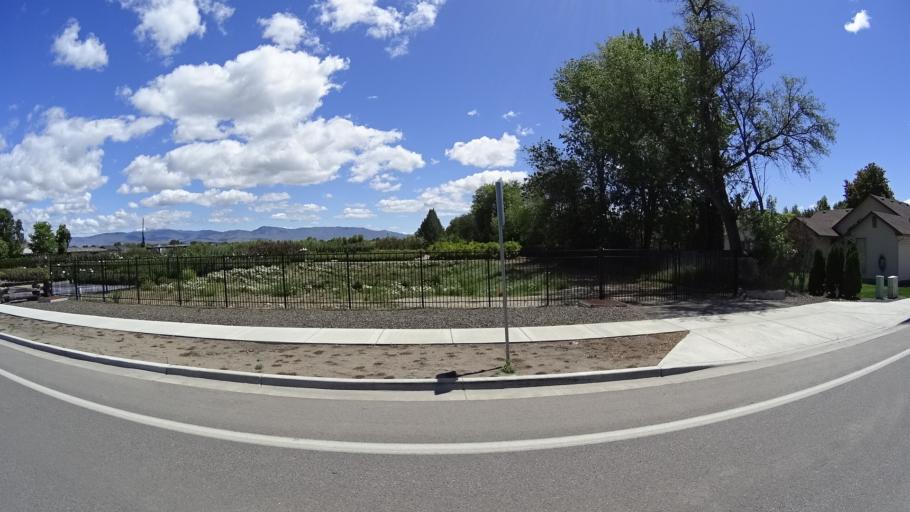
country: US
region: Idaho
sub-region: Ada County
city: Meridian
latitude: 43.6267
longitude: -116.3343
